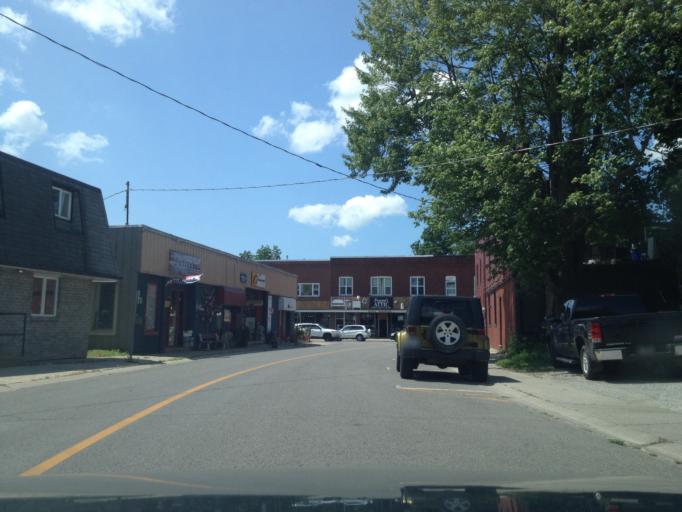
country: CA
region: Ontario
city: Norfolk County
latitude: 42.6240
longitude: -80.4495
